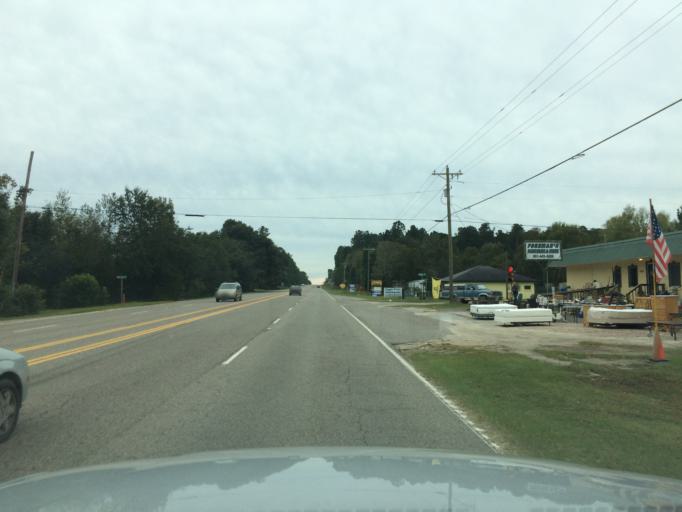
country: US
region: South Carolina
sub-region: Aiken County
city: New Ellenton
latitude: 33.4463
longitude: -81.6867
